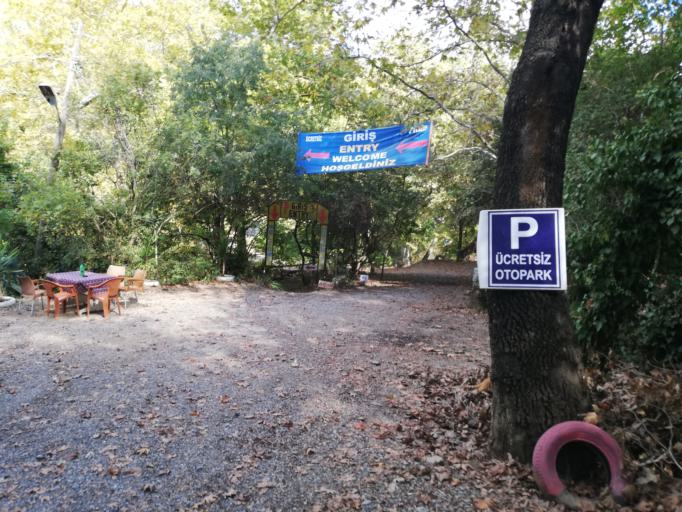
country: TR
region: Antalya
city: Guzelbag
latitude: 36.6687
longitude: 31.8910
